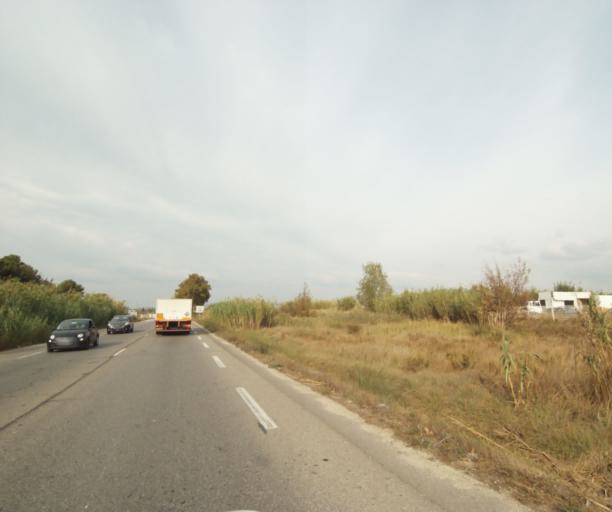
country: FR
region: Provence-Alpes-Cote d'Azur
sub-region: Departement des Bouches-du-Rhone
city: Marignane
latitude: 43.3988
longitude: 5.1994
